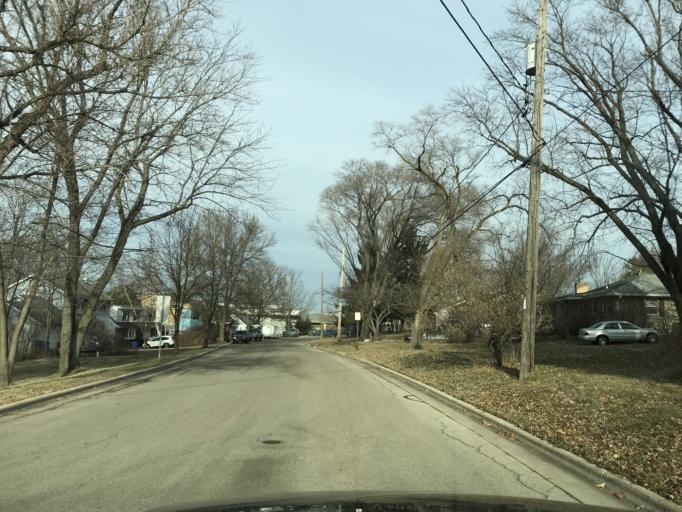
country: US
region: Wisconsin
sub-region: Dane County
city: Monona
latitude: 43.0614
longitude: -89.3412
